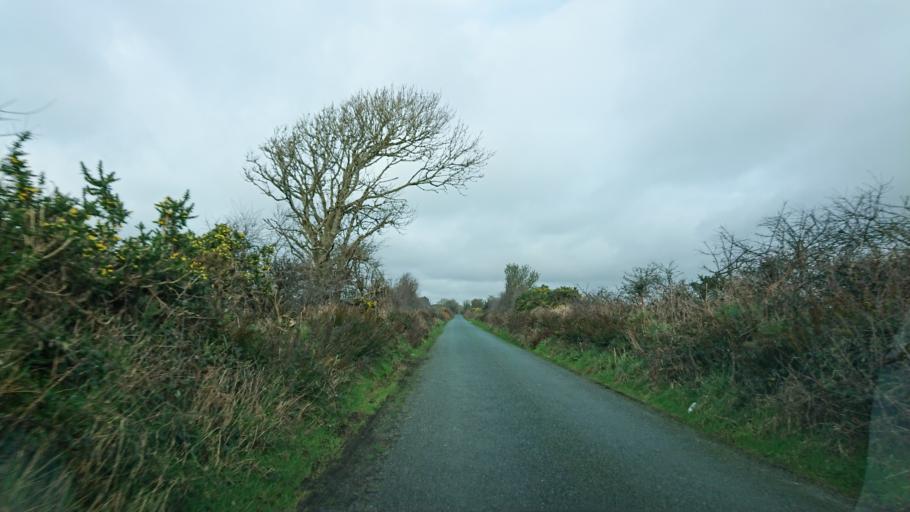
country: IE
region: Munster
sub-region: Waterford
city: Portlaw
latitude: 52.1582
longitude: -7.3078
